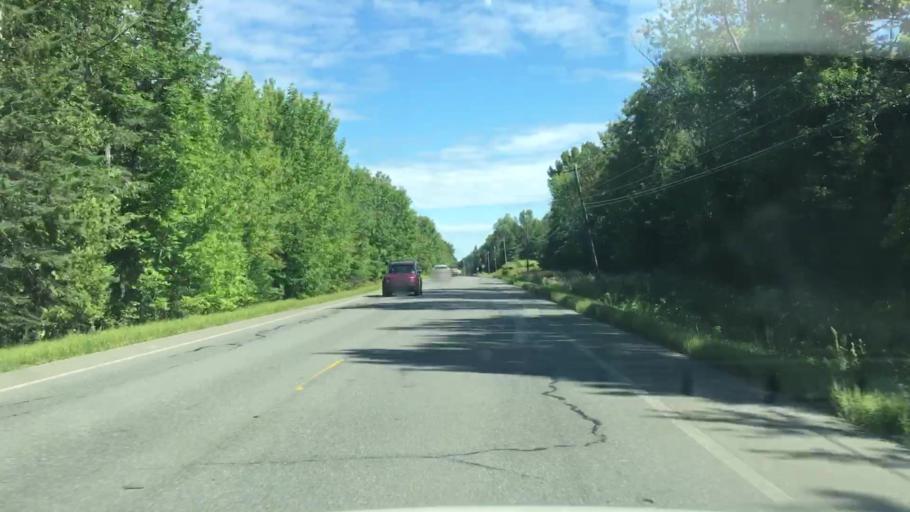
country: US
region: Maine
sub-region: Penobscot County
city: Dexter
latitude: 45.0645
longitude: -69.2448
